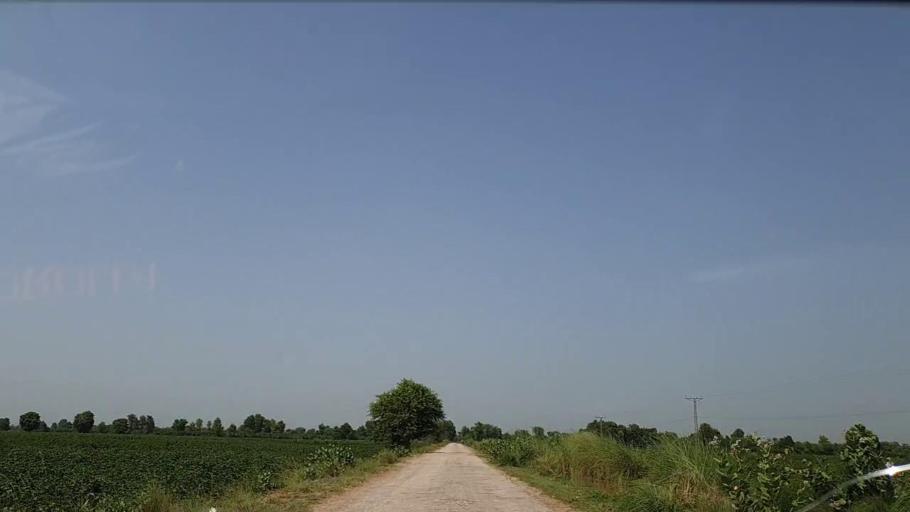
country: PK
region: Sindh
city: Kandiaro
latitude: 27.0357
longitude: 68.1566
